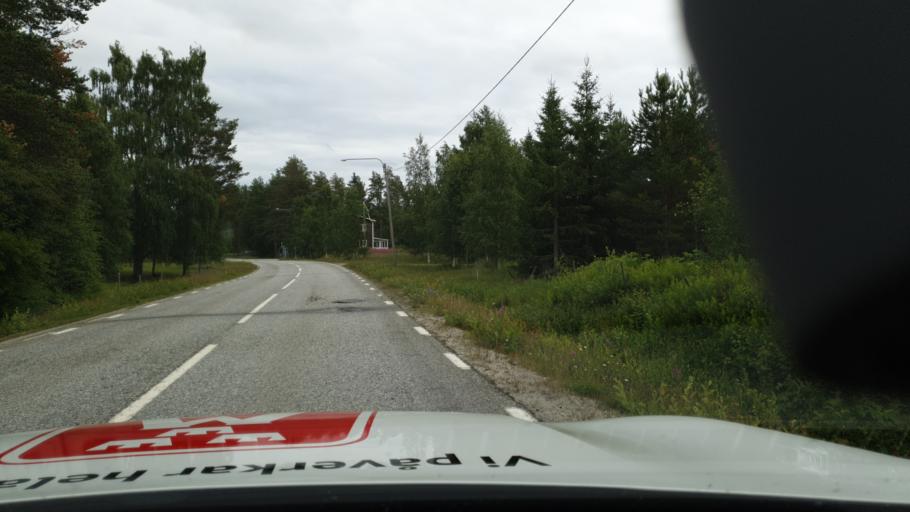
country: SE
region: Vaesterbotten
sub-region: Lycksele Kommun
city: Soderfors
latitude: 64.6263
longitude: 18.0697
